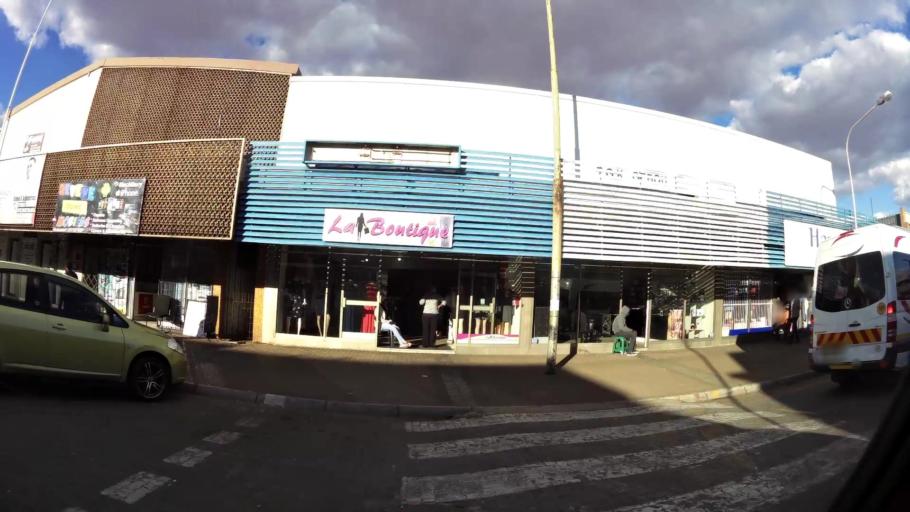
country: ZA
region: North-West
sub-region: Dr Kenneth Kaunda District Municipality
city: Potchefstroom
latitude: -26.7104
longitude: 27.0974
